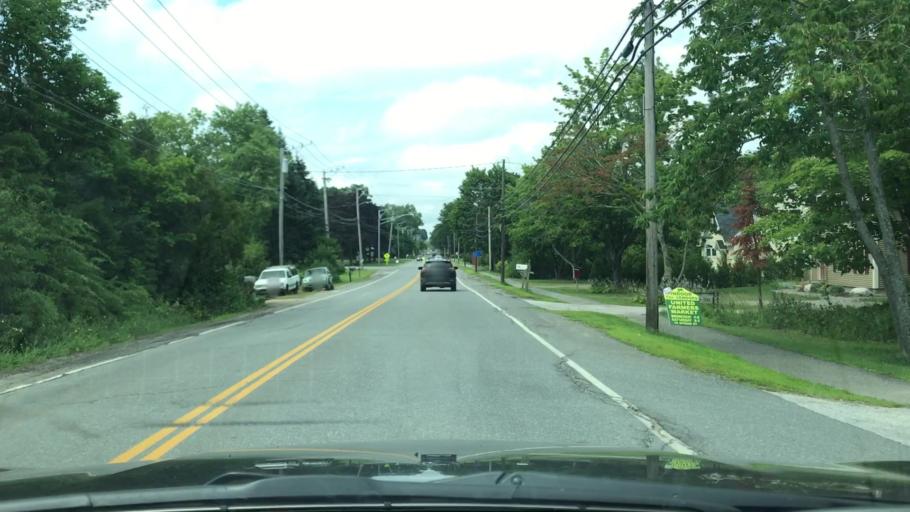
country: US
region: Maine
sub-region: Waldo County
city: Belfast
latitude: 44.4134
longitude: -68.9954
